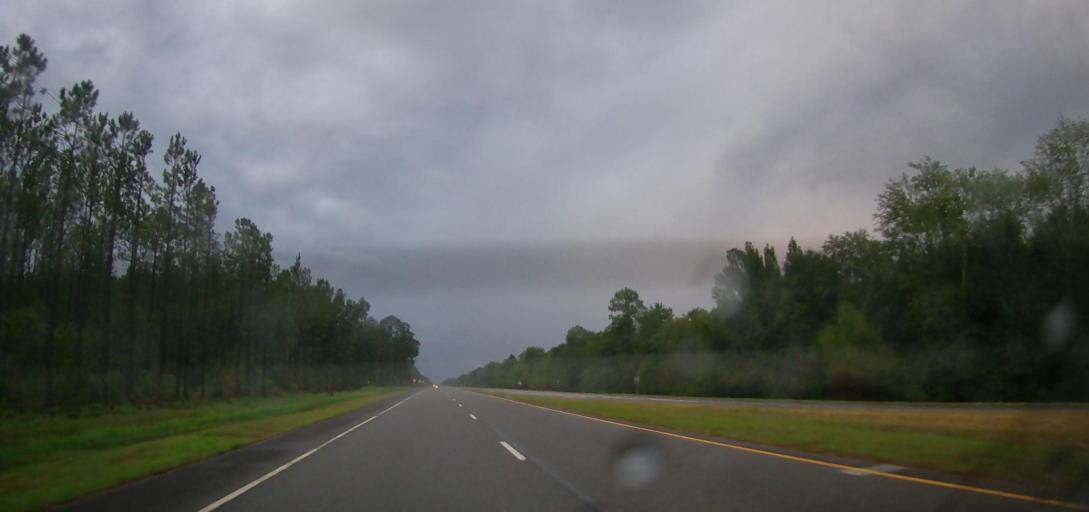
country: US
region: Georgia
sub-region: Lanier County
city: Lakeland
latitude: 30.9483
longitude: -82.9759
